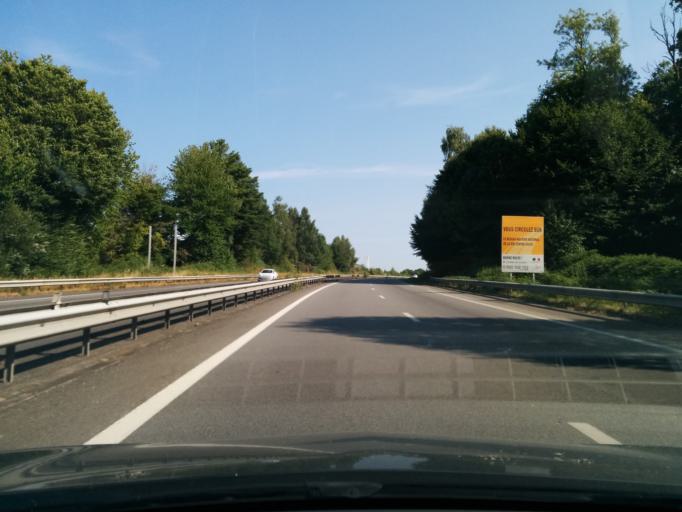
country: FR
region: Limousin
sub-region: Departement de la Haute-Vienne
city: Boisseuil
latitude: 45.7634
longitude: 1.3290
